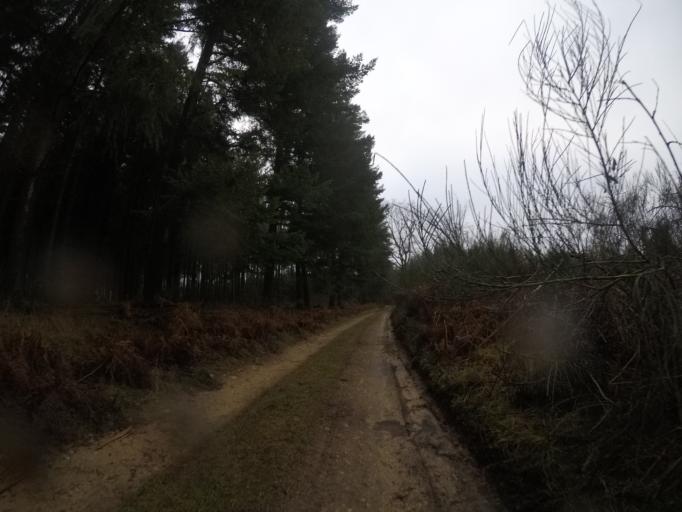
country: BE
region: Wallonia
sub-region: Province du Luxembourg
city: Fauvillers
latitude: 49.8092
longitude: 5.6127
